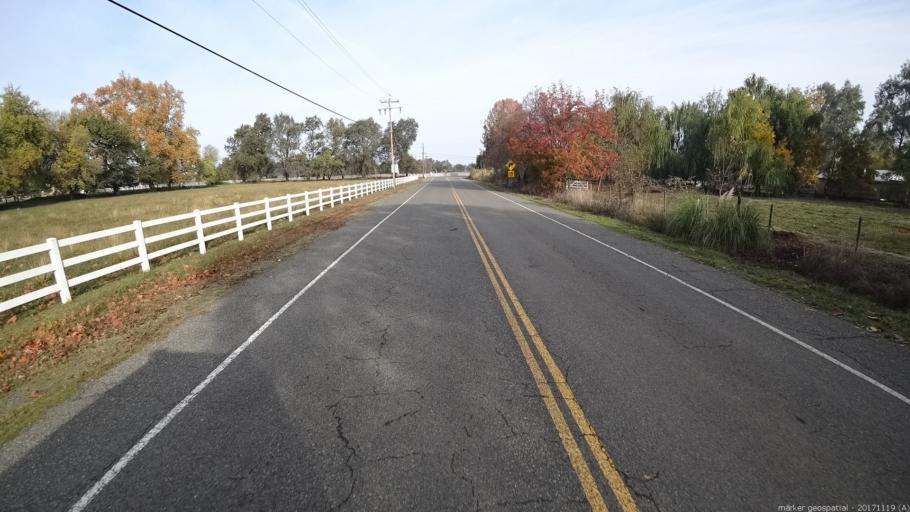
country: US
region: California
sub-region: Shasta County
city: Redding
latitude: 40.5189
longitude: -122.3493
